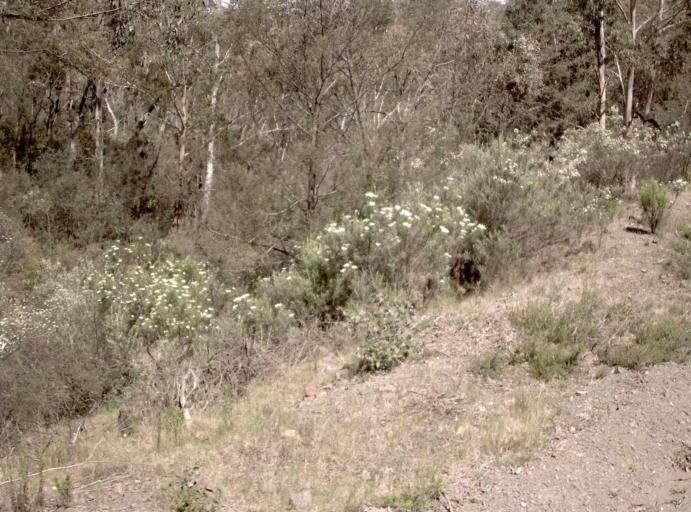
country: AU
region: New South Wales
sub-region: Bombala
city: Bombala
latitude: -37.1029
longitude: 148.6360
